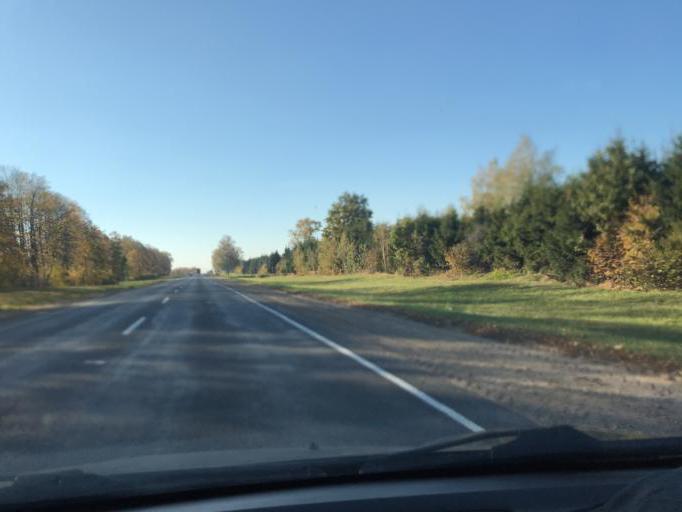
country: BY
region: Minsk
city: Urechcha
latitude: 53.0745
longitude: 27.7650
